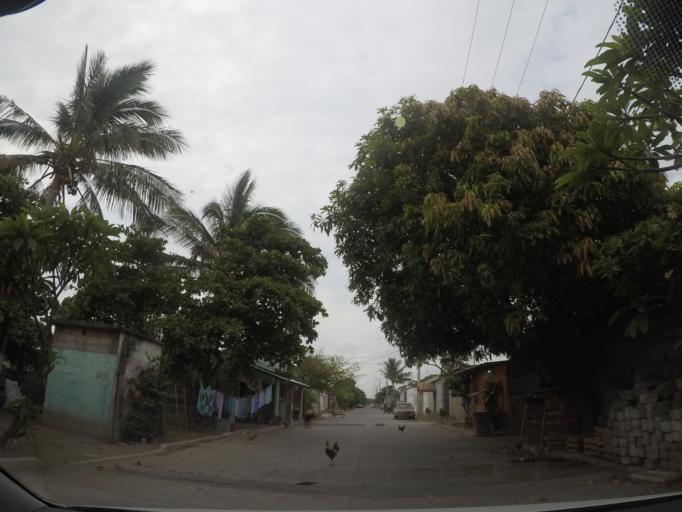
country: MX
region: Oaxaca
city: Juchitan de Zaragoza
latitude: 16.4572
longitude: -95.0156
